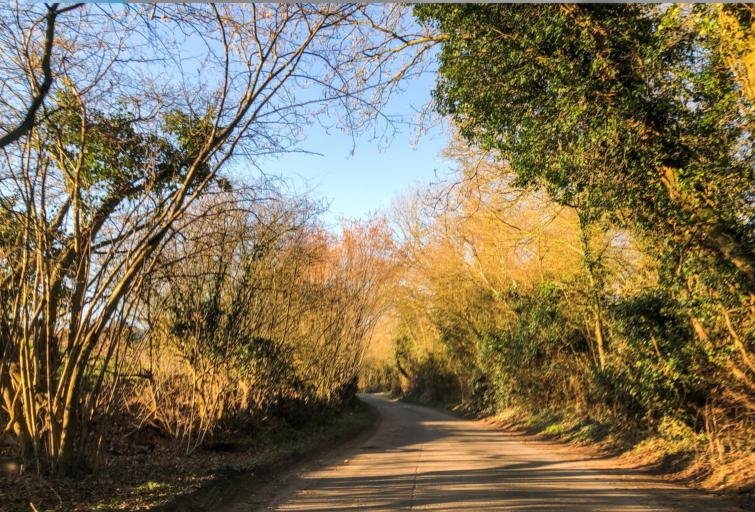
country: GB
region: England
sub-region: Warwickshire
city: Wroxall
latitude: 52.2754
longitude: -1.6656
